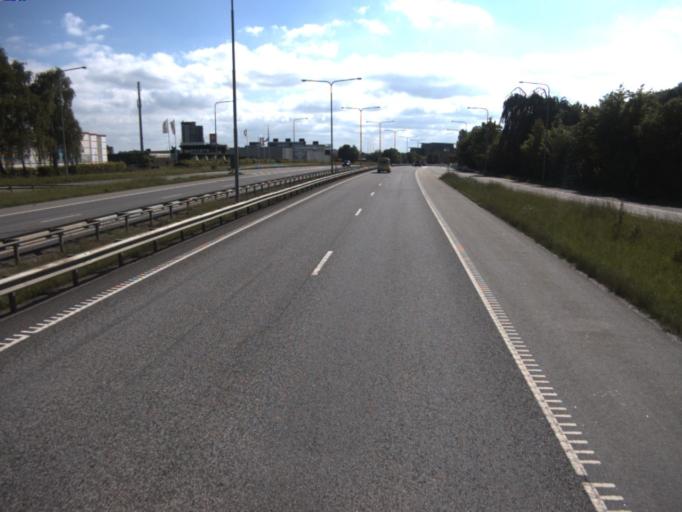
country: SE
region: Skane
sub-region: Helsingborg
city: Helsingborg
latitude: 56.0663
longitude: 12.7189
